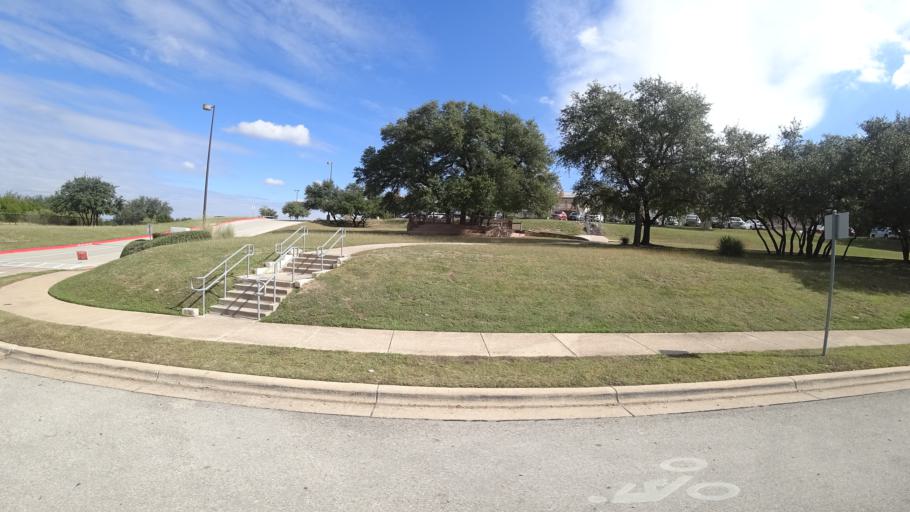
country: US
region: Texas
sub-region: Travis County
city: Hudson Bend
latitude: 30.3659
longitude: -97.9014
